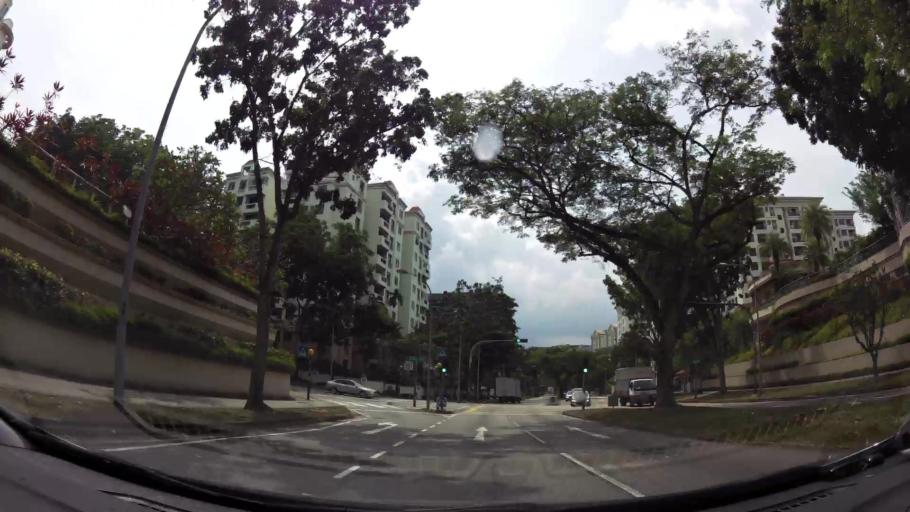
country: MY
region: Johor
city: Johor Bahru
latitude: 1.3591
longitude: 103.7638
